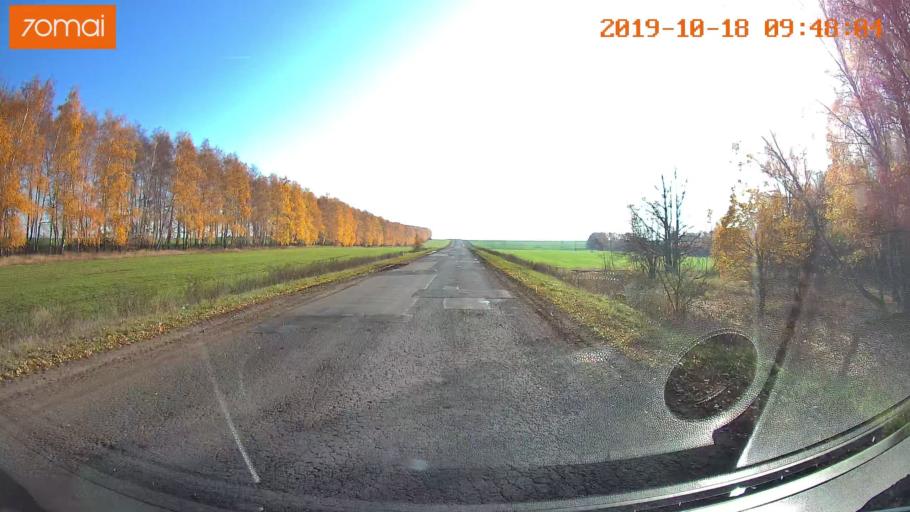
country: RU
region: Tula
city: Kazachka
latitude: 53.3195
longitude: 38.2411
